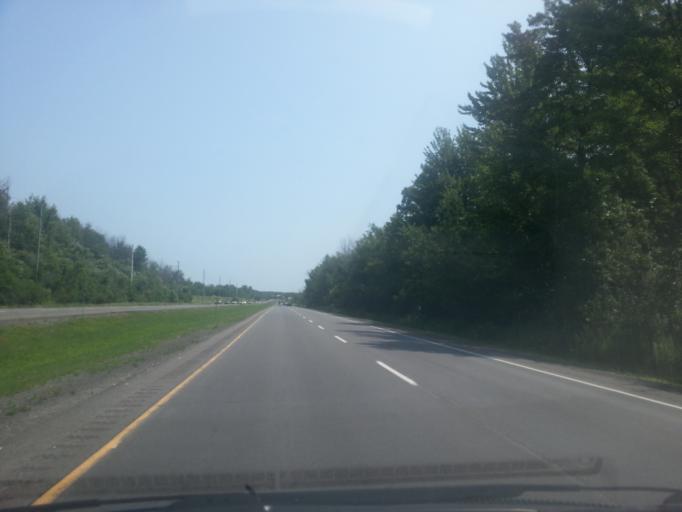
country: CA
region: Ontario
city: Ottawa
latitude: 45.4280
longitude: -75.5611
